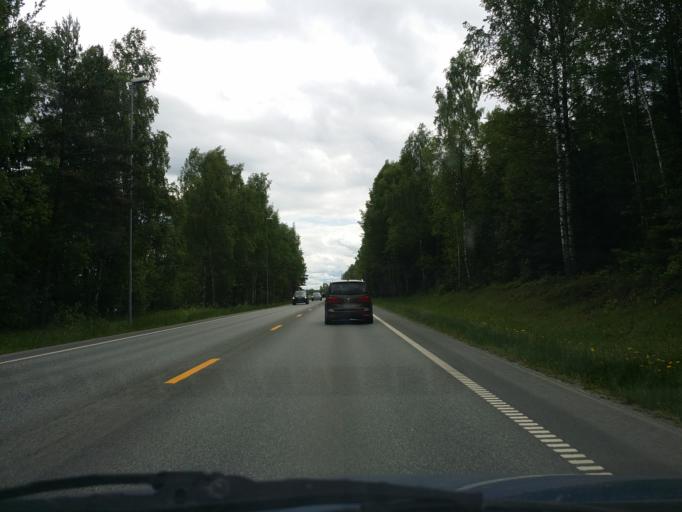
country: NO
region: Hedmark
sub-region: Stange
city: Stange
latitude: 60.7527
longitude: 11.1960
